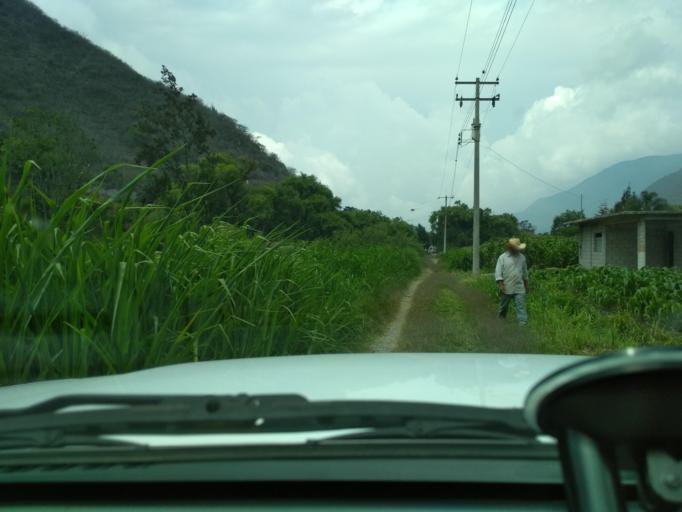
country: MX
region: Veracruz
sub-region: Nogales
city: Taza de Agua Ojo Zarco
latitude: 18.7817
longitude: -97.2135
